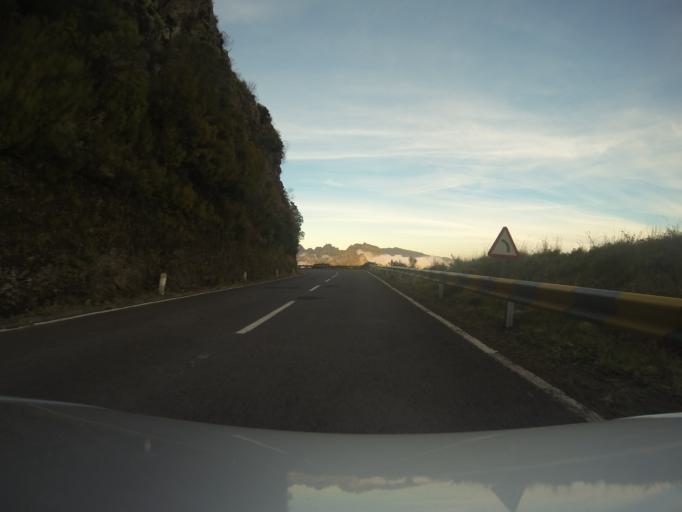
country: PT
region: Madeira
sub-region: Sao Vicente
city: Sao Vicente
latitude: 32.7377
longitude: -17.0500
